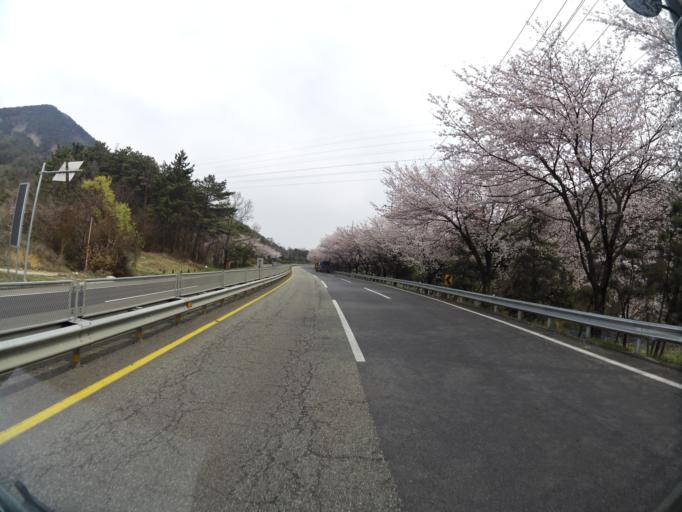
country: KR
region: Gyeongsangnam-do
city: Changnyeong
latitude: 35.4448
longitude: 128.5412
